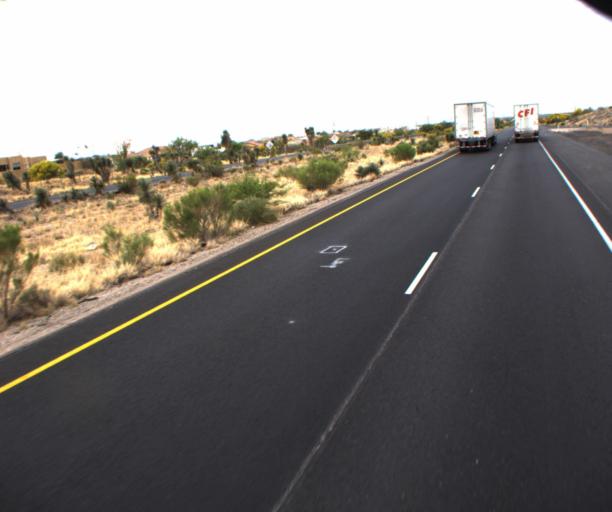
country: US
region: Arizona
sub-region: Pima County
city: Vail
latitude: 32.0096
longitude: -110.6939
